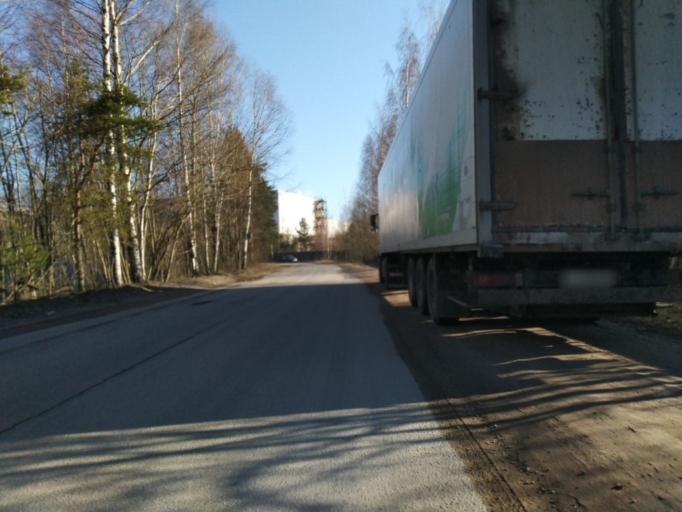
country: RU
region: Leningrad
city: Novoye Devyatkino
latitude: 60.0689
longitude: 30.4801
